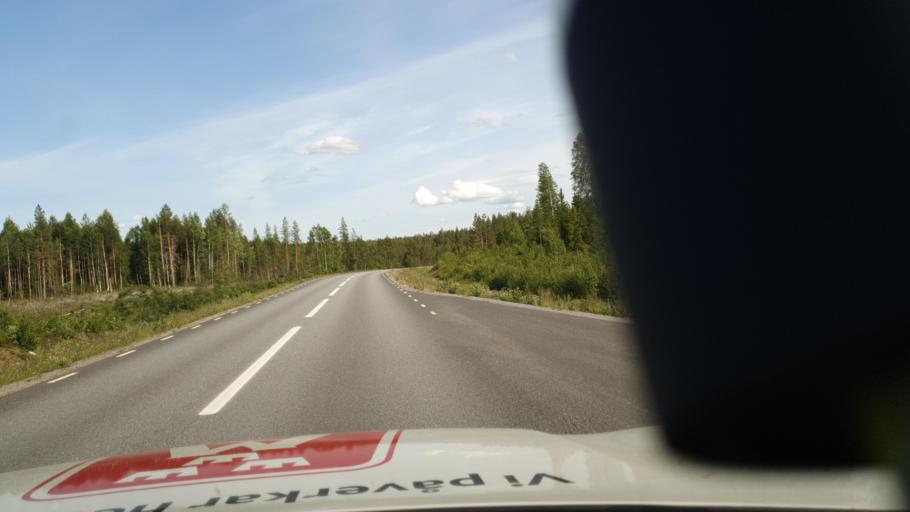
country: SE
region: Vaesterbotten
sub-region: Skelleftea Kommun
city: Forsbacka
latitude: 64.7332
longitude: 20.3867
